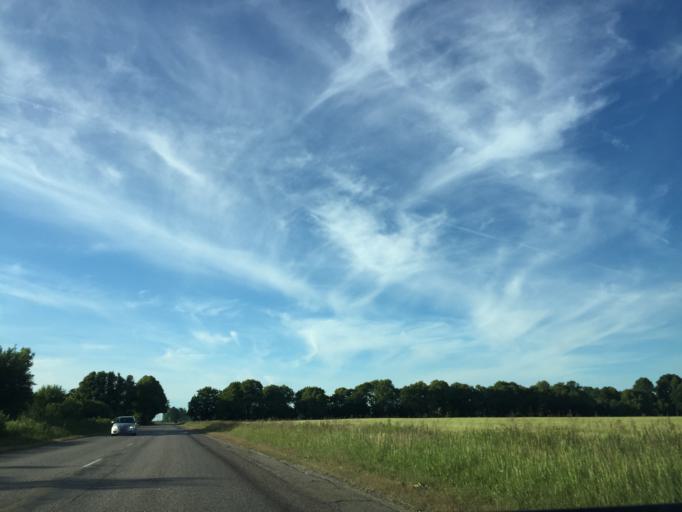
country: LV
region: Ventspils
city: Ventspils
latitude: 57.3291
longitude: 21.5641
